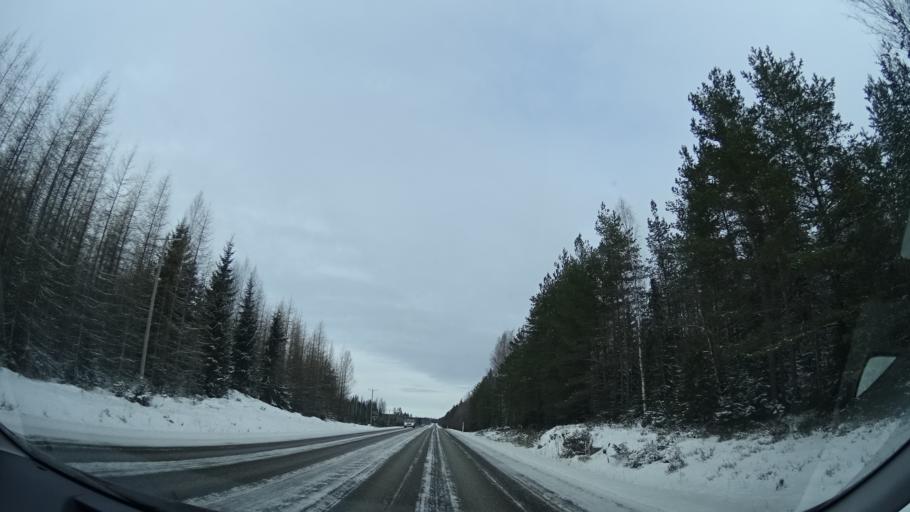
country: FI
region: Uusimaa
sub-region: Helsinki
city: Kaerkoelae
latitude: 60.6695
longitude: 23.8286
